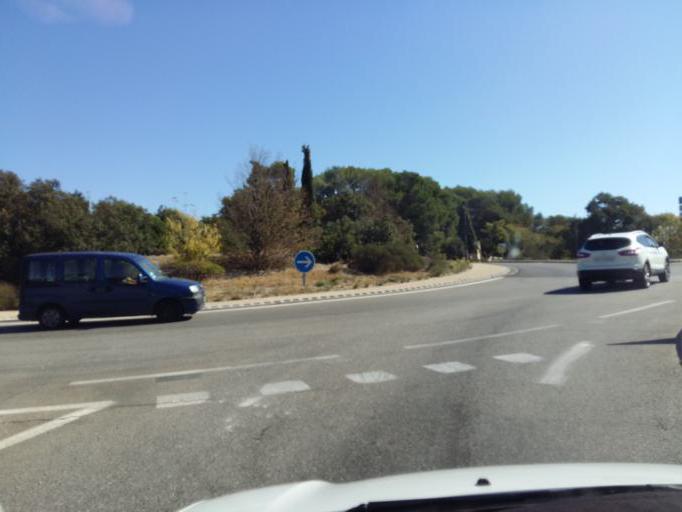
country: FR
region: Provence-Alpes-Cote d'Azur
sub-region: Departement des Bouches-du-Rhone
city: Mallemort
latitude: 43.7541
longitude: 5.1807
